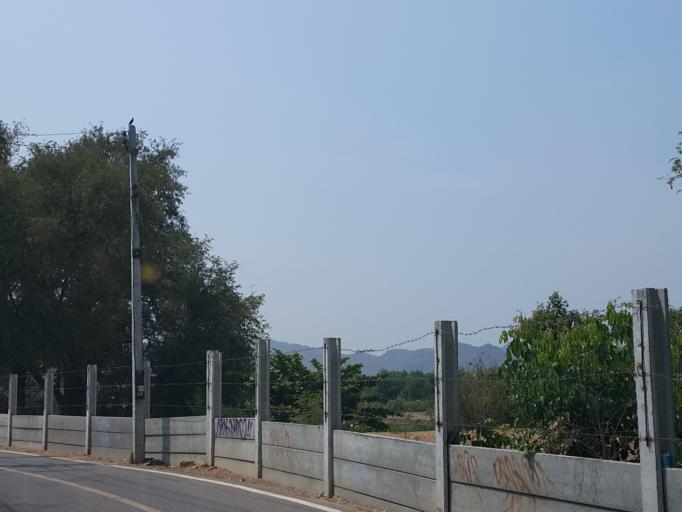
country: TH
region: Kanchanaburi
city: Kanchanaburi
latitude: 14.0311
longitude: 99.5215
